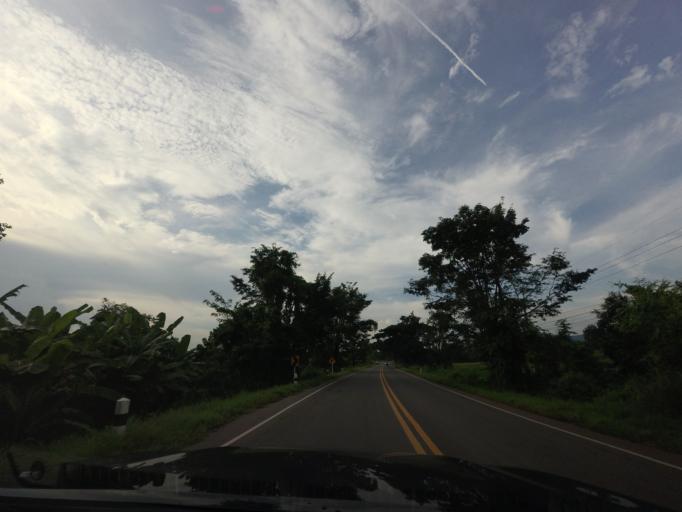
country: TH
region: Changwat Udon Thani
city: Nam Som
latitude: 17.8094
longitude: 102.2710
